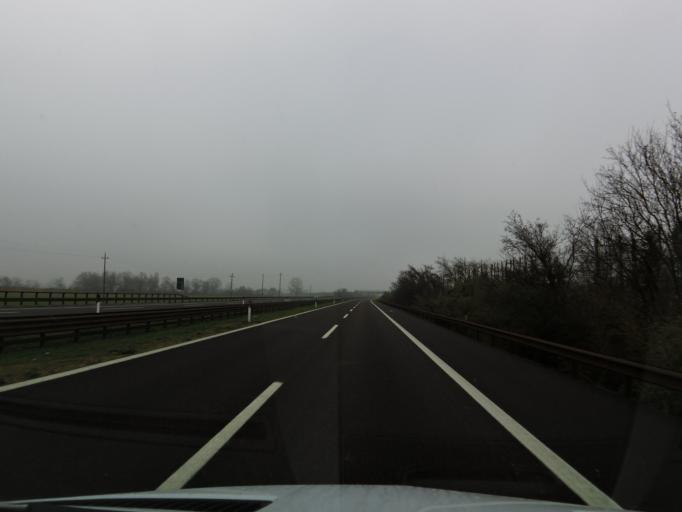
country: IT
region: Lombardy
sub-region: Provincia di Mantova
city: Bondeno
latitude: 44.9641
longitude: 10.8596
